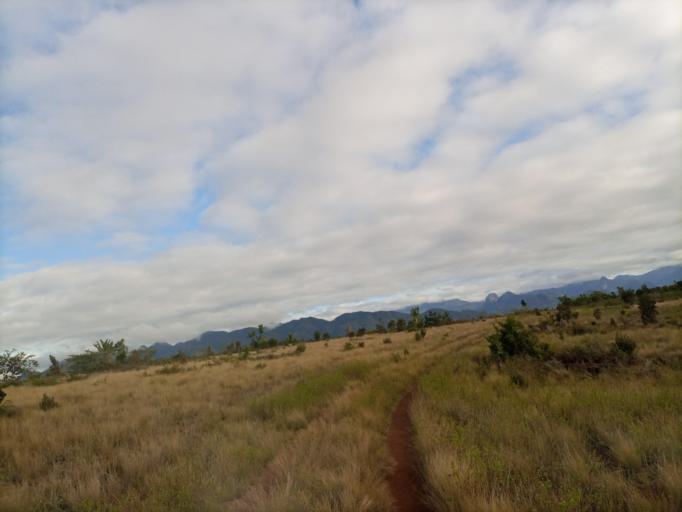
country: MG
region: Anosy
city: Fort Dauphin
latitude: -24.3101
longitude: 47.2494
